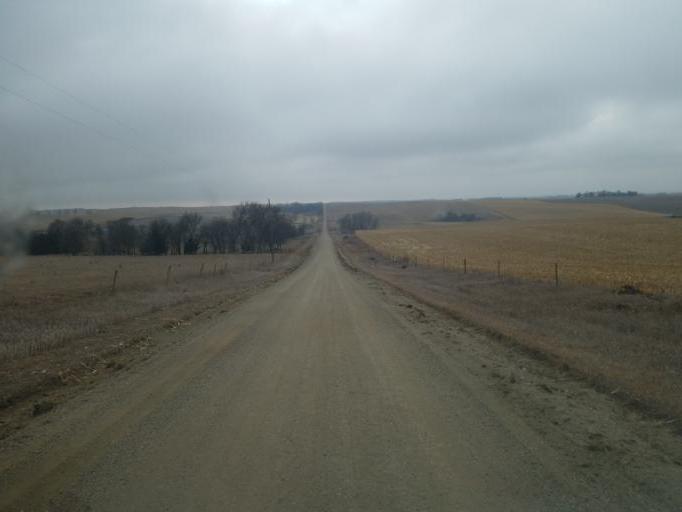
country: US
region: Nebraska
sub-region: Knox County
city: Creighton
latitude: 42.4948
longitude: -97.7984
